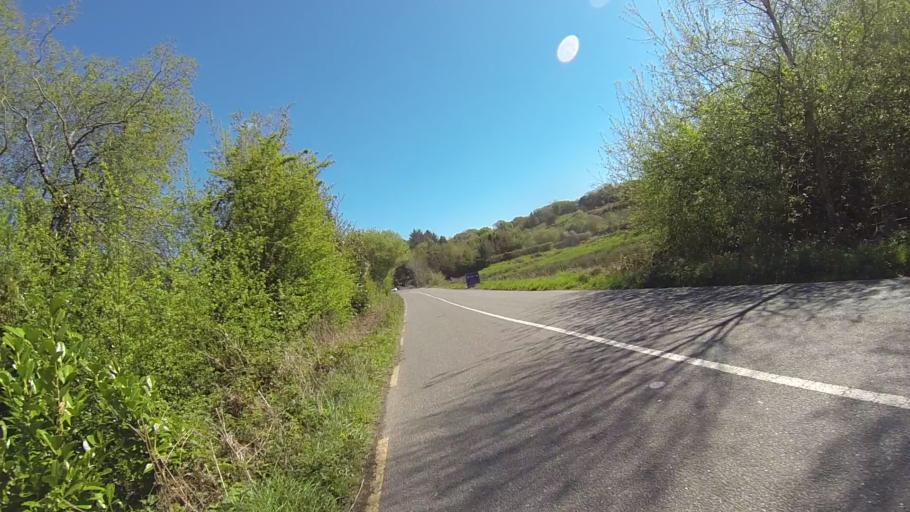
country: IE
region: Munster
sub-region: Ciarrai
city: Kenmare
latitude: 51.8521
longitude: -9.6285
